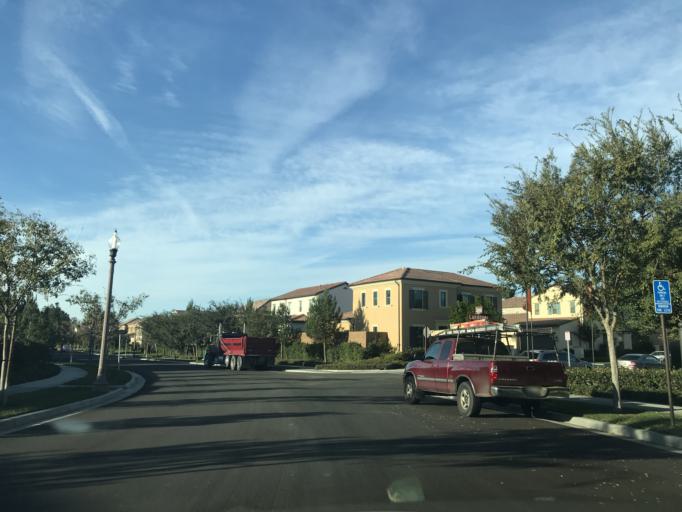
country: US
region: California
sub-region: Orange County
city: North Tustin
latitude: 33.7114
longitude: -117.7526
